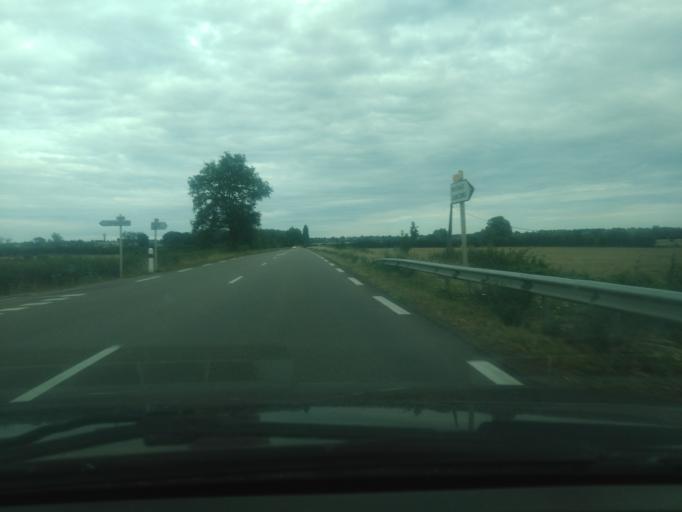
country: FR
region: Bourgogne
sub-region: Departement de la Nievre
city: Saint-Pierre-le-Moutier
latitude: 46.8037
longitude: 3.0883
